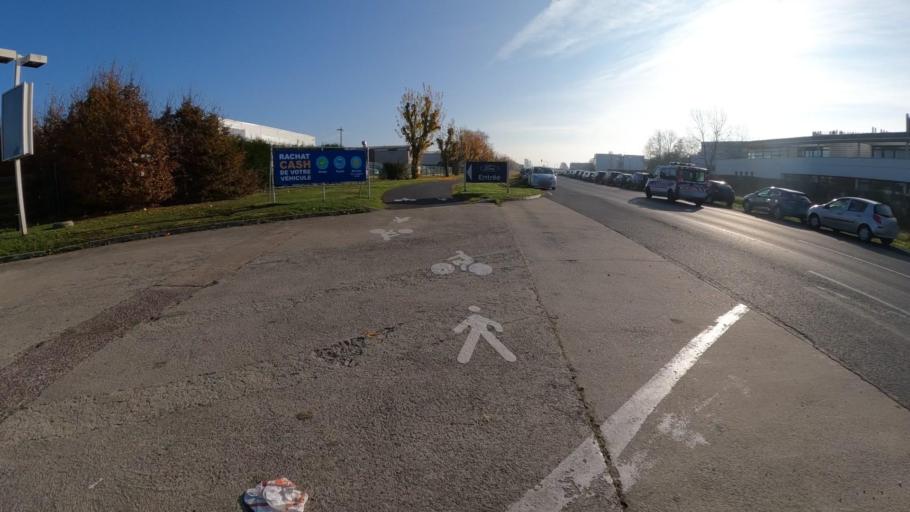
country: FR
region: Lower Normandy
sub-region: Departement du Calvados
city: Epron
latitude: 49.2107
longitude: -0.3539
